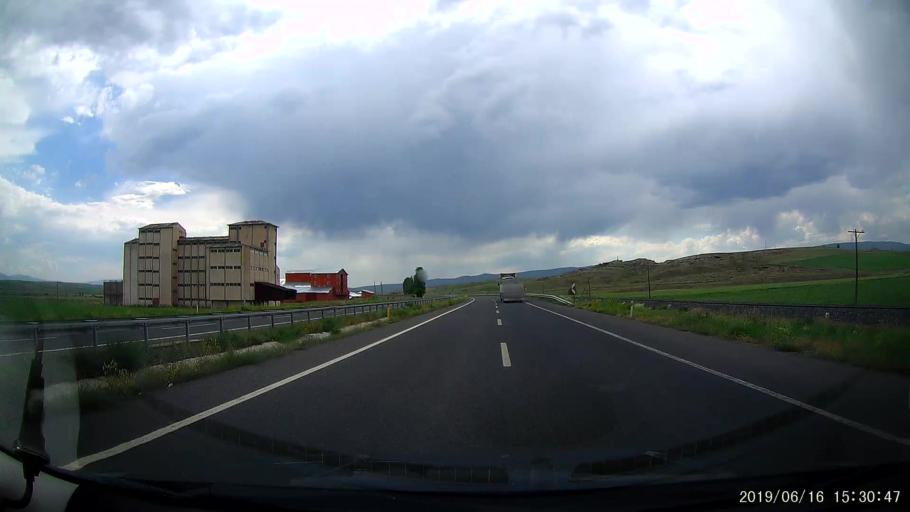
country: TR
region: Erzurum
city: Horasan
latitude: 40.0343
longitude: 42.0956
